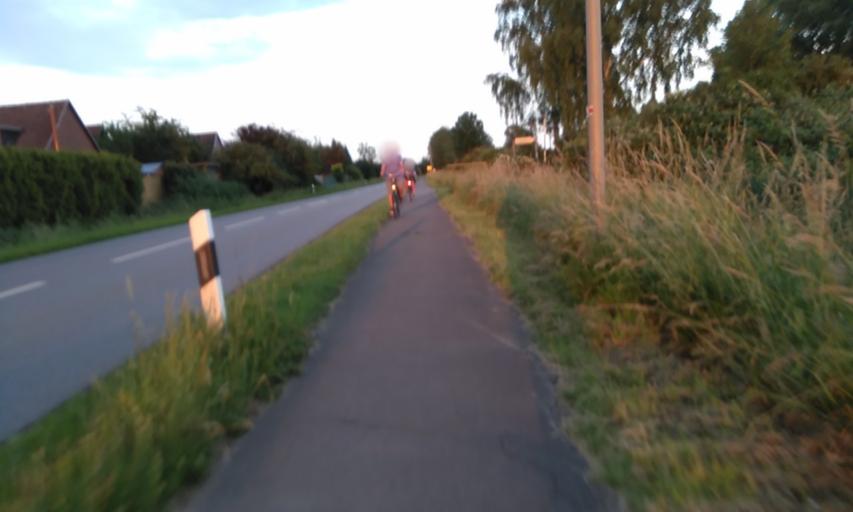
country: DE
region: Lower Saxony
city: Jork
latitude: 53.5095
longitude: 9.7251
